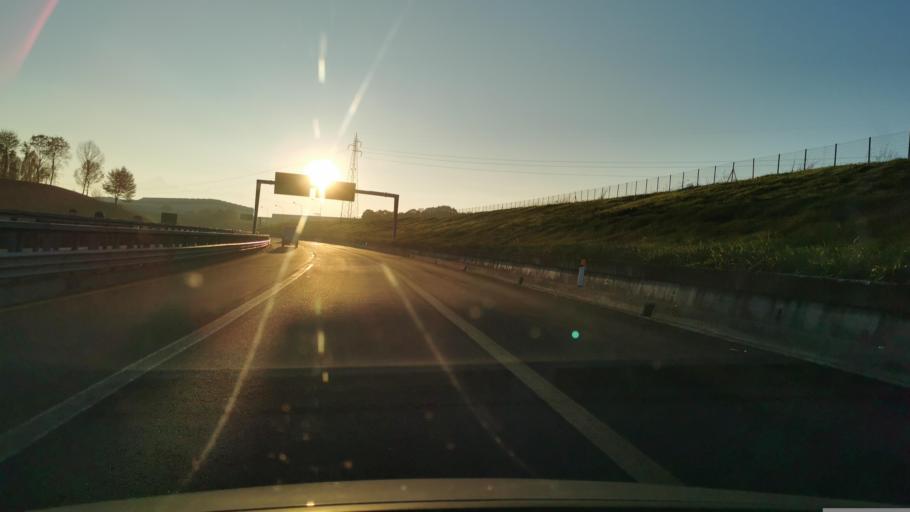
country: IT
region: Piedmont
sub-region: Provincia di Torino
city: Borgo Melano
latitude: 45.0070
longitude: 7.5688
